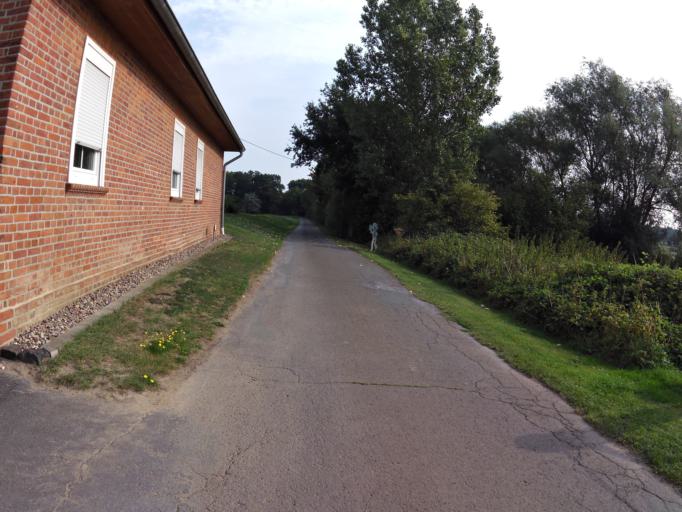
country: DE
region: Lower Saxony
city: Raddestorf
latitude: 52.4498
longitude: 9.0084
